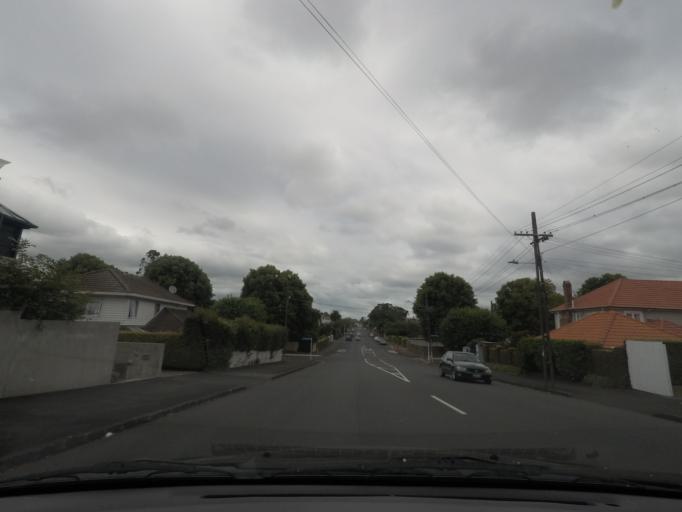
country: NZ
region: Auckland
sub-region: Auckland
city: Auckland
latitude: -36.8804
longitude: 174.7920
